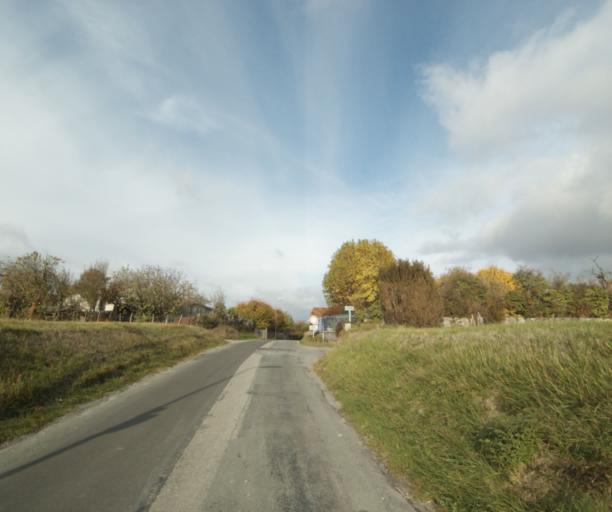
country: FR
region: Poitou-Charentes
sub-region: Departement de la Charente-Maritime
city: Saint-Georges-des-Coteaux
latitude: 45.7602
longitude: -0.7118
